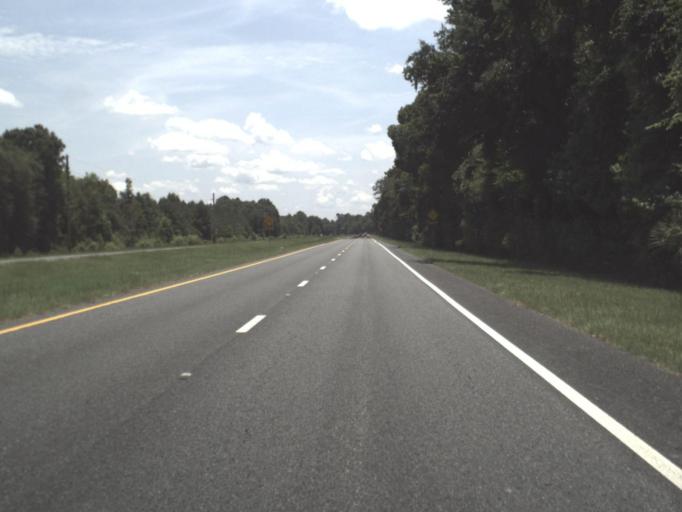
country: US
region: Florida
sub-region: Taylor County
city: Steinhatchee
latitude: 29.6881
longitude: -83.2696
